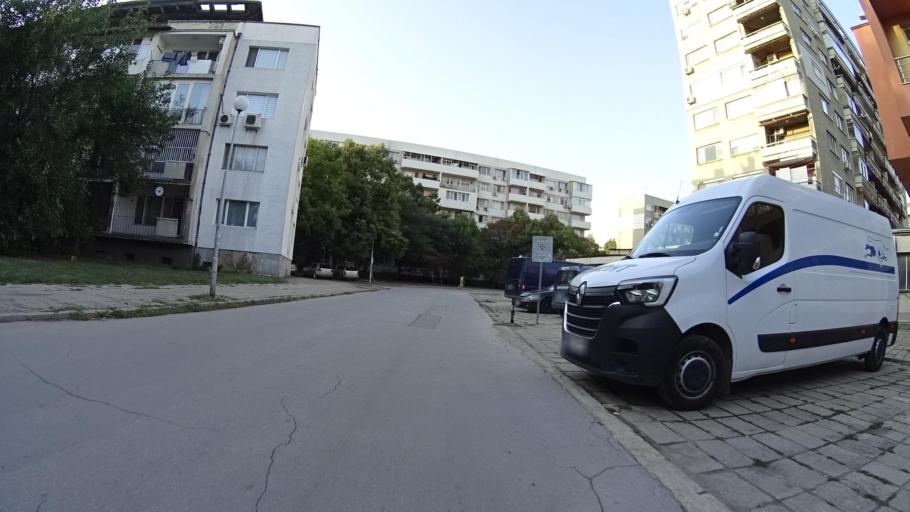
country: BG
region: Plovdiv
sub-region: Obshtina Plovdiv
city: Plovdiv
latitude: 42.1323
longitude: 24.7458
